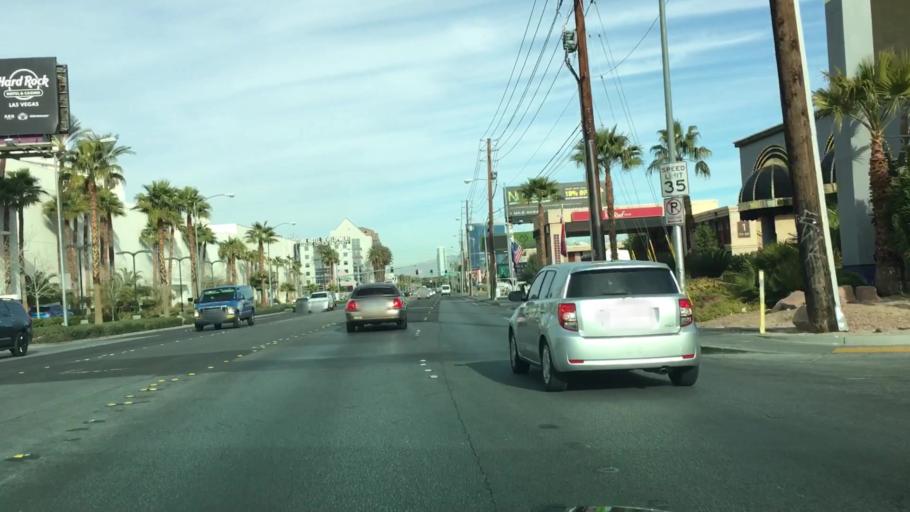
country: US
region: Nevada
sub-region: Clark County
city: Paradise
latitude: 36.1092
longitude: -115.1524
